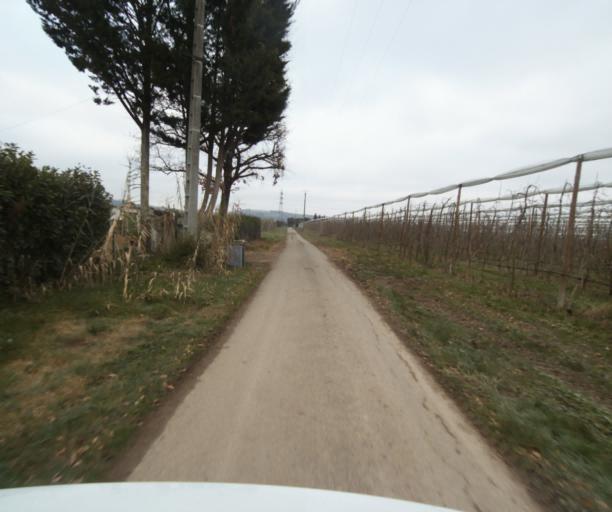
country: FR
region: Midi-Pyrenees
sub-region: Departement du Tarn-et-Garonne
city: Moissac
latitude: 44.1048
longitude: 1.1331
